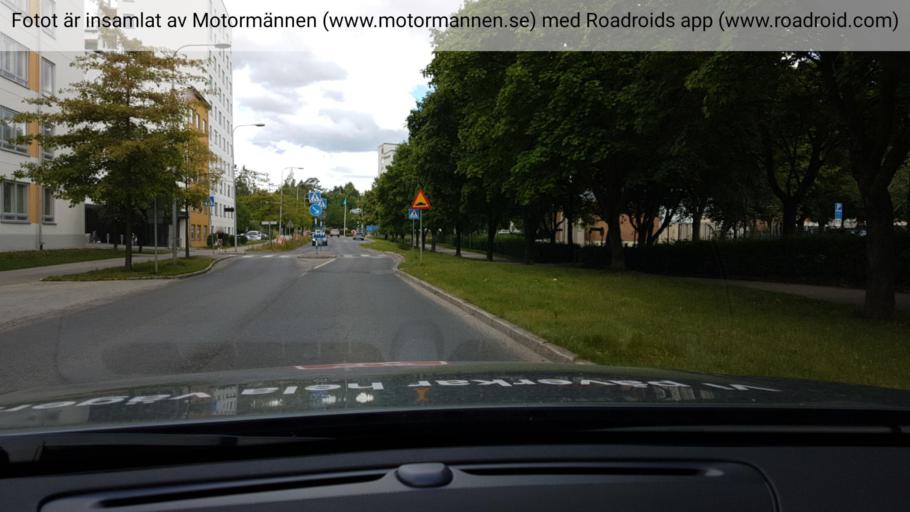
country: SE
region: Stockholm
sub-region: Huddinge Kommun
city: Huddinge
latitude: 59.2420
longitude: 17.9953
